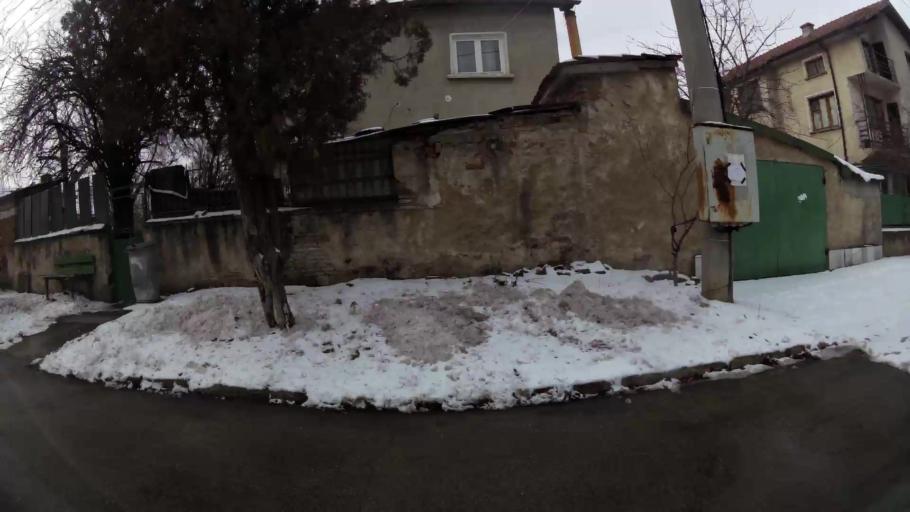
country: BG
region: Sofia-Capital
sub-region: Stolichna Obshtina
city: Sofia
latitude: 42.7143
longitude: 23.4015
